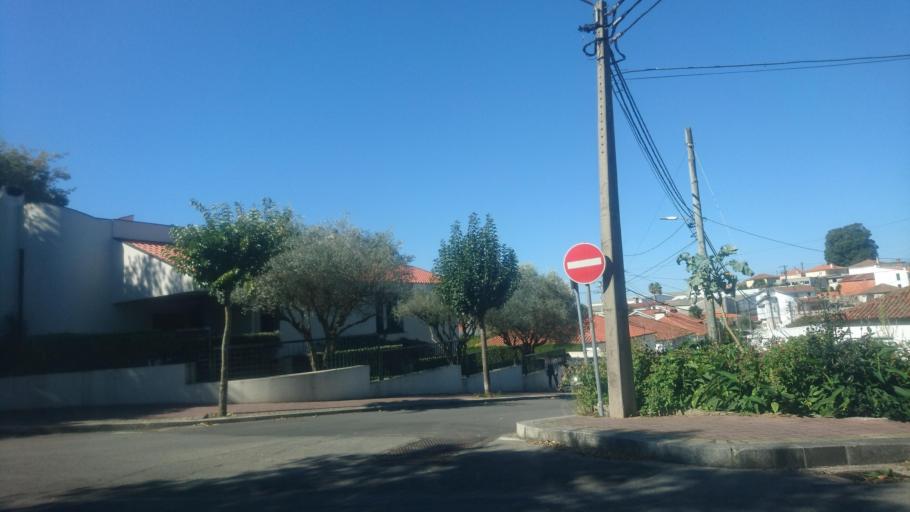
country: PT
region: Aveiro
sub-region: Santa Maria da Feira
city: Lamas
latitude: 40.9800
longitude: -8.5725
